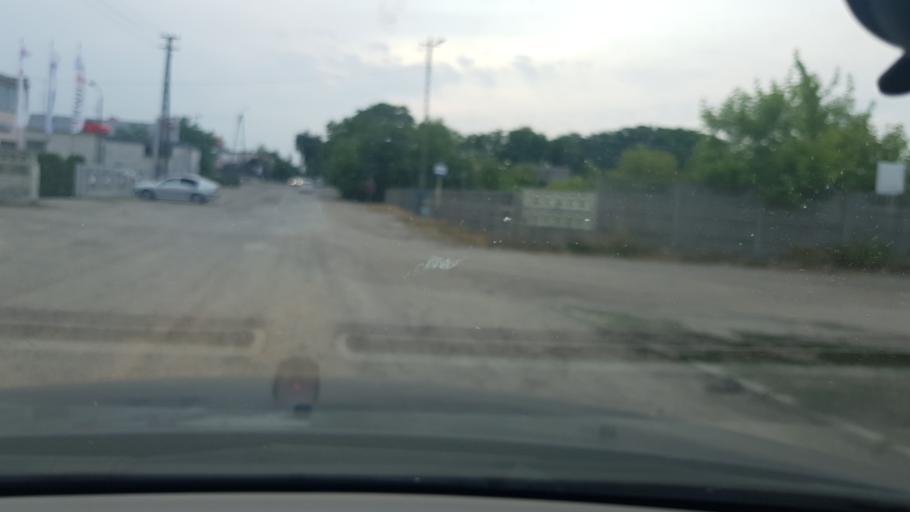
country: PL
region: Lodz Voivodeship
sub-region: Powiat tomaszowski
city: Tomaszow Mazowiecki
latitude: 51.5538
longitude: 20.0194
